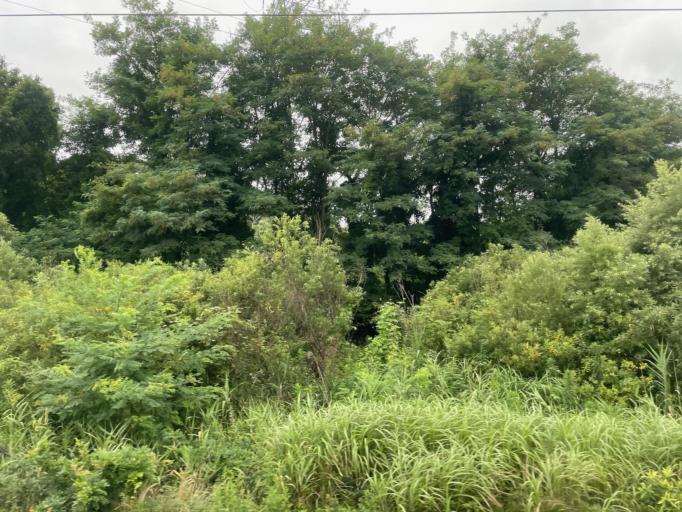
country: JP
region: Fukushima
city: Koriyama
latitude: 37.4512
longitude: 140.3837
